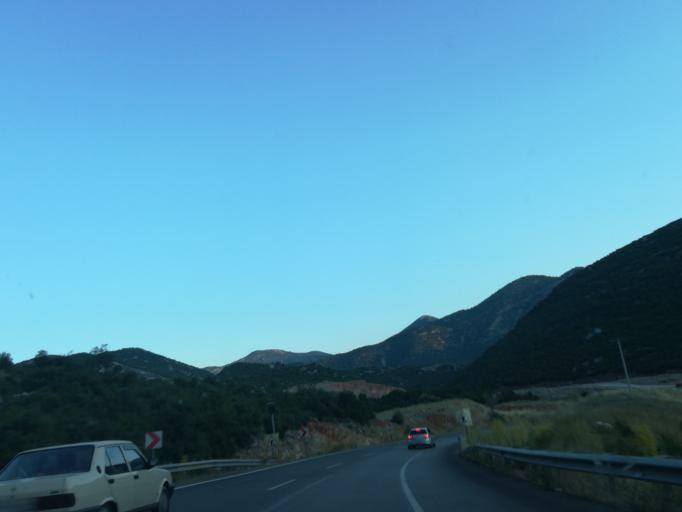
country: TR
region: Antalya
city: Dagbeli
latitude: 37.1594
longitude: 30.5108
